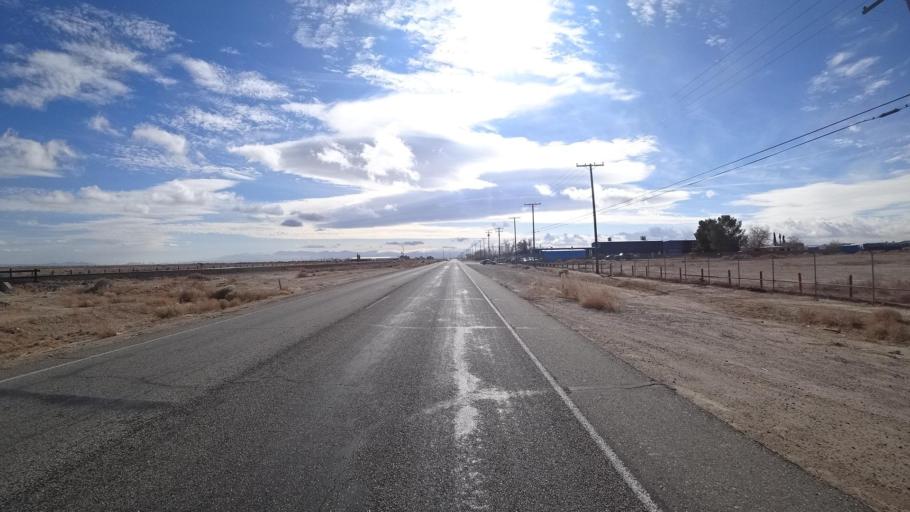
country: US
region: California
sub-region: Kern County
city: Rosamond
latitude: 34.8463
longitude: -118.1602
